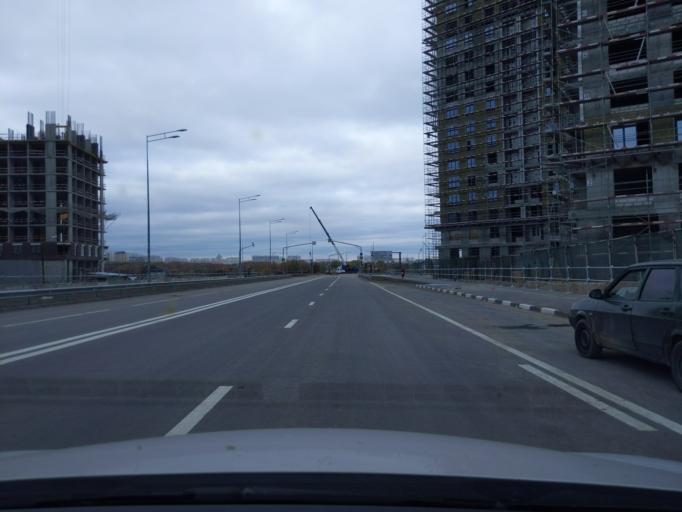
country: RU
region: Moscow
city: Strogino
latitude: 55.8162
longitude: 37.4276
